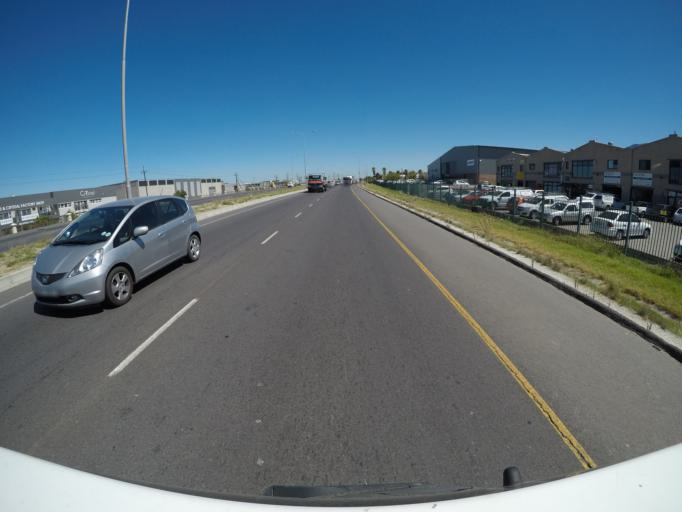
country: ZA
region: Western Cape
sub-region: Overberg District Municipality
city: Grabouw
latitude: -34.1048
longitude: 18.8561
